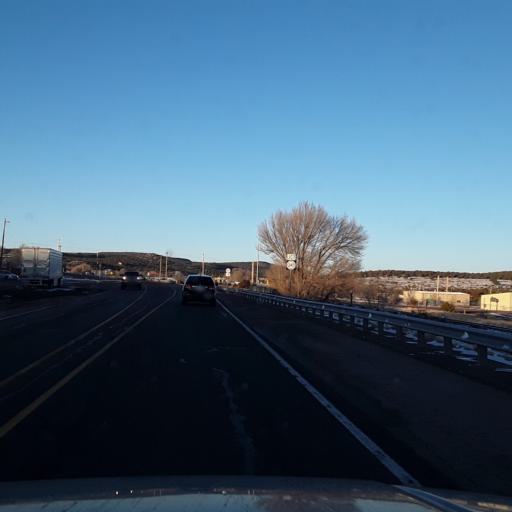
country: US
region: New Mexico
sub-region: Lincoln County
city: Carrizozo
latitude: 34.2434
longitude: -105.5957
